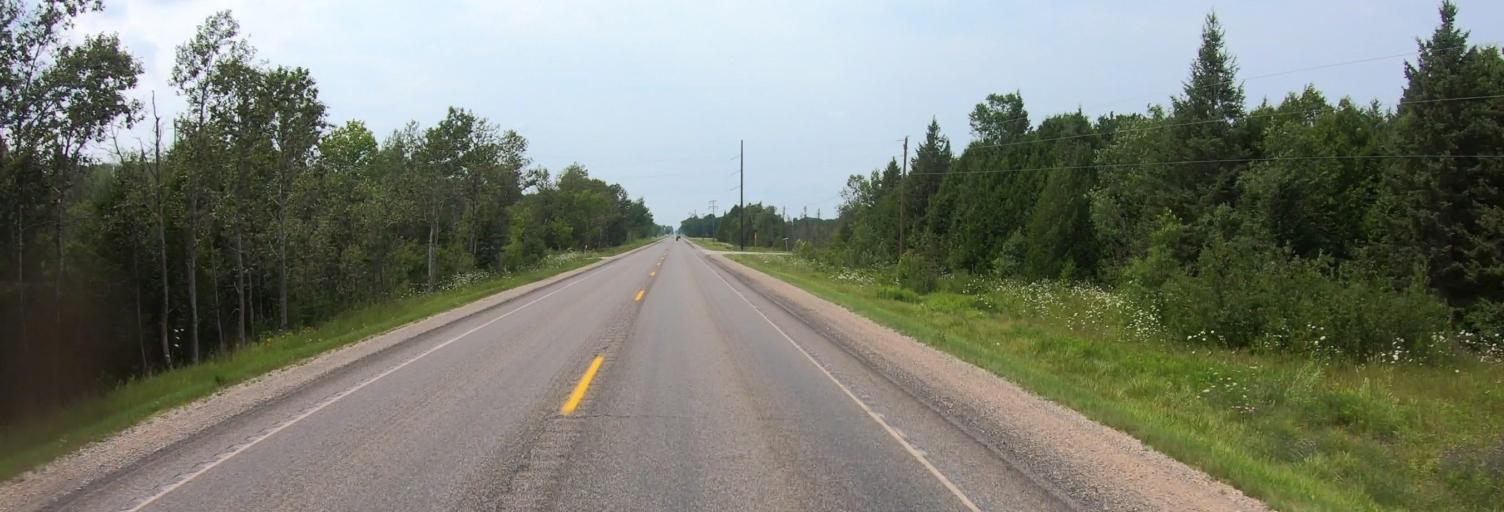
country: US
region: Michigan
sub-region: Alger County
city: Munising
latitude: 46.3330
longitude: -86.9069
